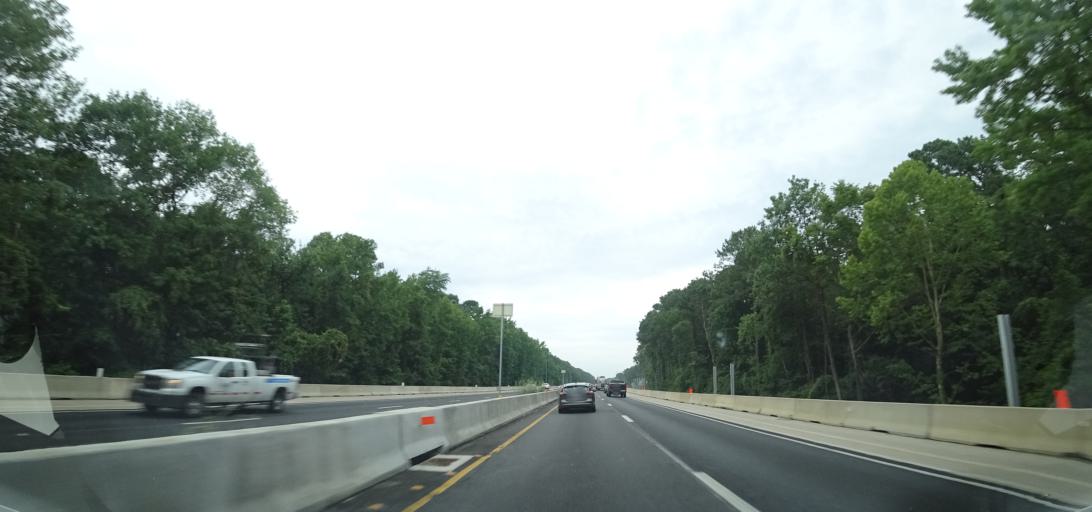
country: US
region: Virginia
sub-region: York County
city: Yorktown
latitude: 37.1422
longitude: -76.5305
